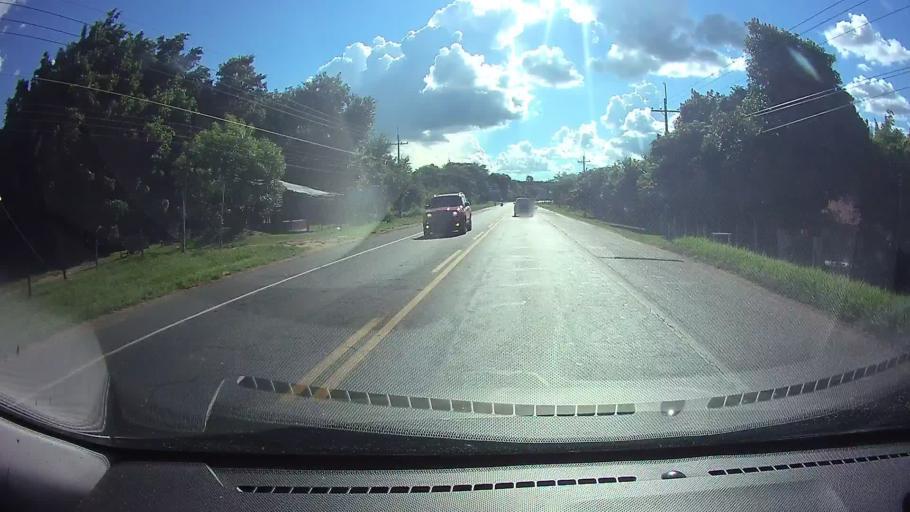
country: PY
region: Cordillera
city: Eusebio Ayala
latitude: -25.3820
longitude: -57.0049
